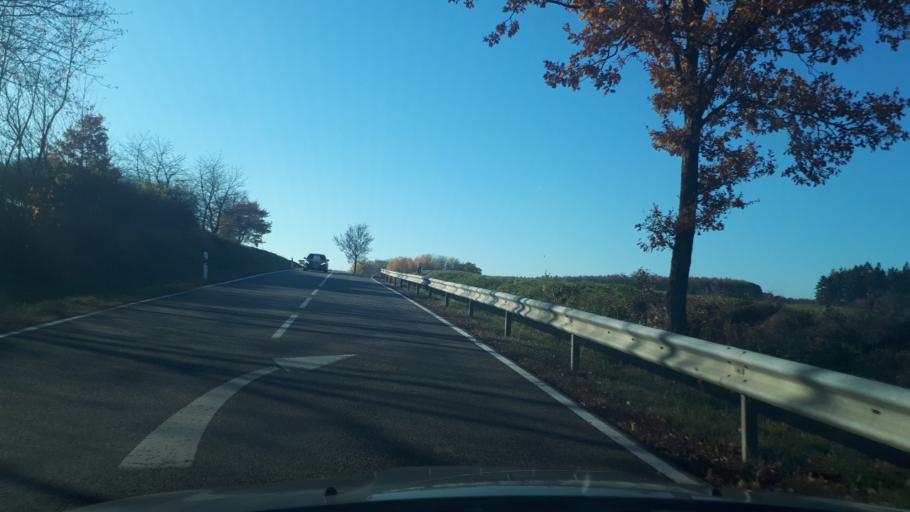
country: DE
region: Rheinland-Pfalz
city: Weiler
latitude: 50.1459
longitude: 7.0697
